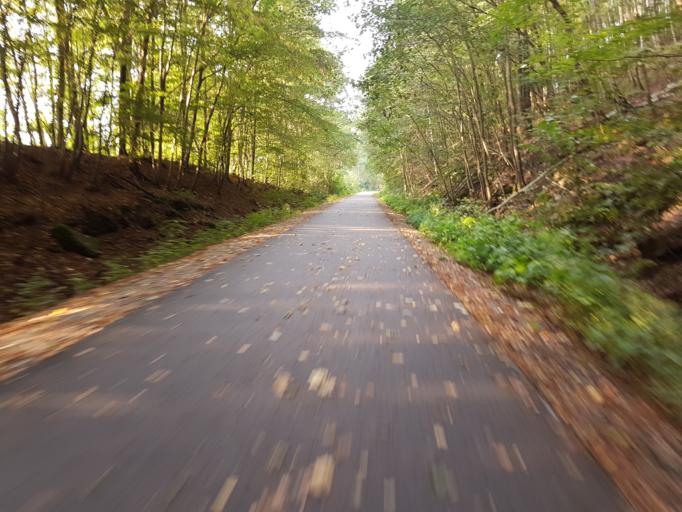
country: DE
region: Saxony
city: Wittgensdorf
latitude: 50.8979
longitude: 12.8950
